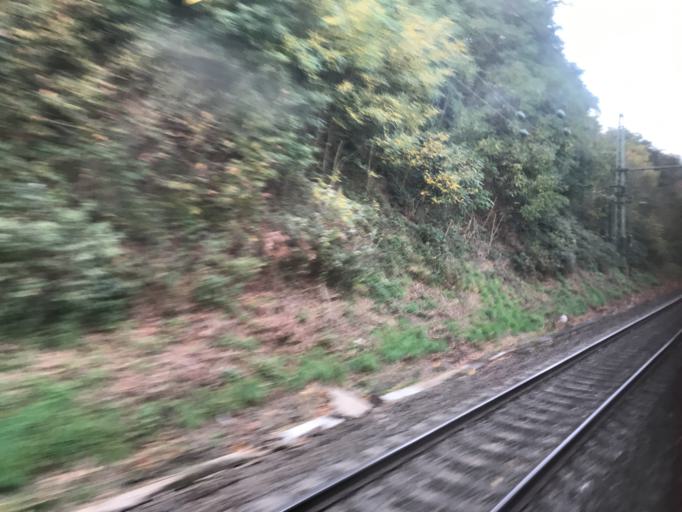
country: DE
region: North Rhine-Westphalia
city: Witten
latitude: 51.4297
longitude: 7.3401
